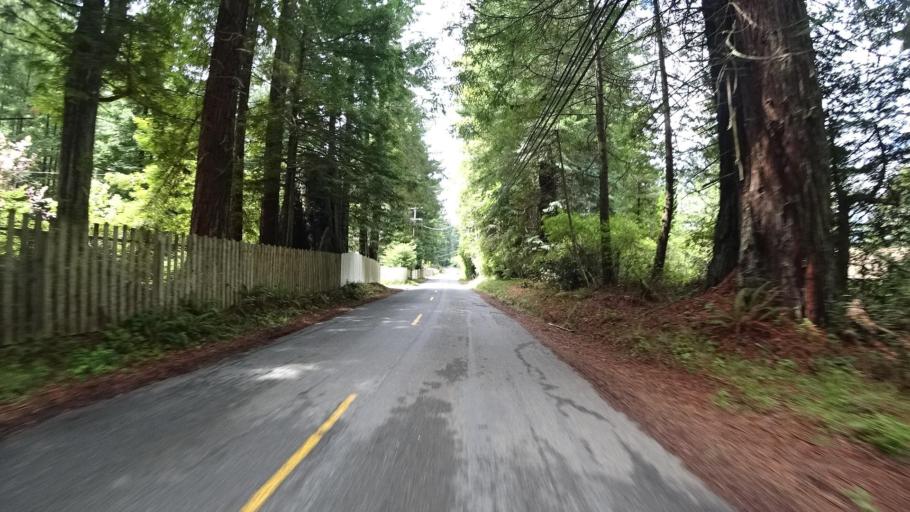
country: US
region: California
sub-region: Humboldt County
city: Bayside
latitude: 40.8006
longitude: -124.0416
